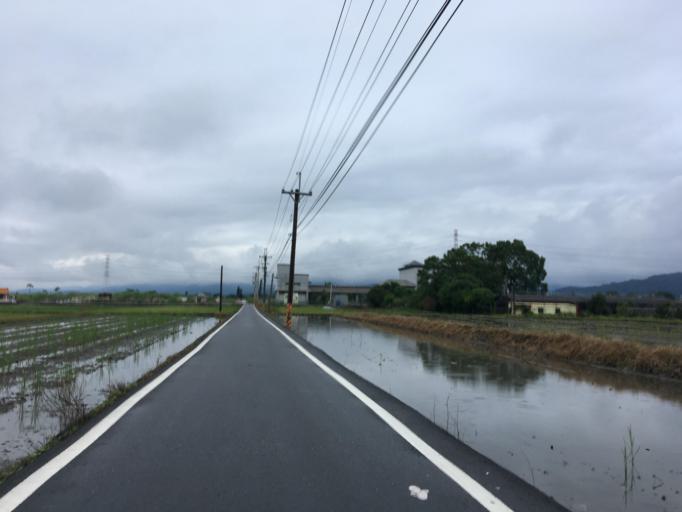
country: TW
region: Taiwan
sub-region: Yilan
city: Yilan
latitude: 24.6645
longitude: 121.7447
